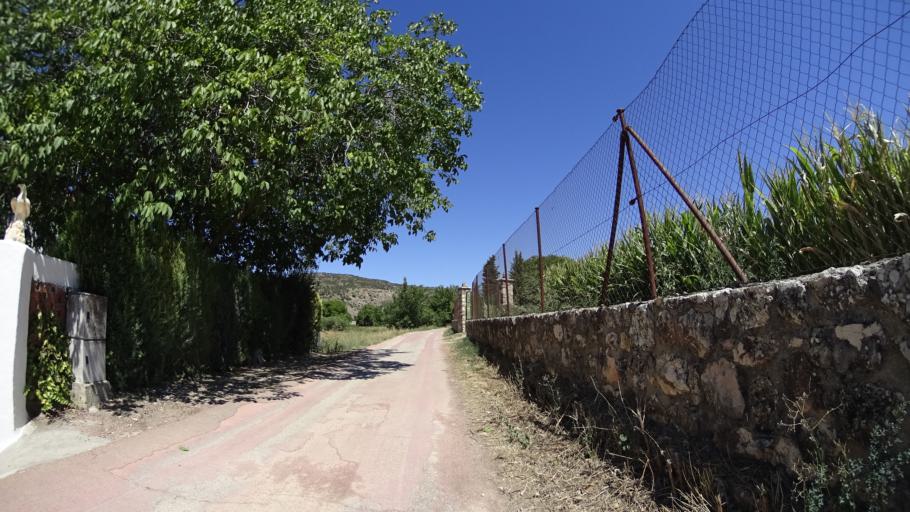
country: ES
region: Madrid
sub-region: Provincia de Madrid
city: Carabana
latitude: 40.2836
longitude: -3.2006
